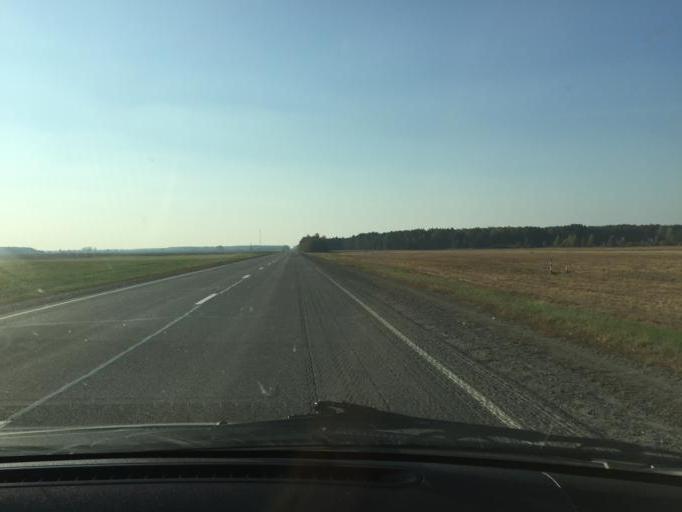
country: BY
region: Brest
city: Davyd-Haradok
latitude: 52.2427
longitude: 27.1768
